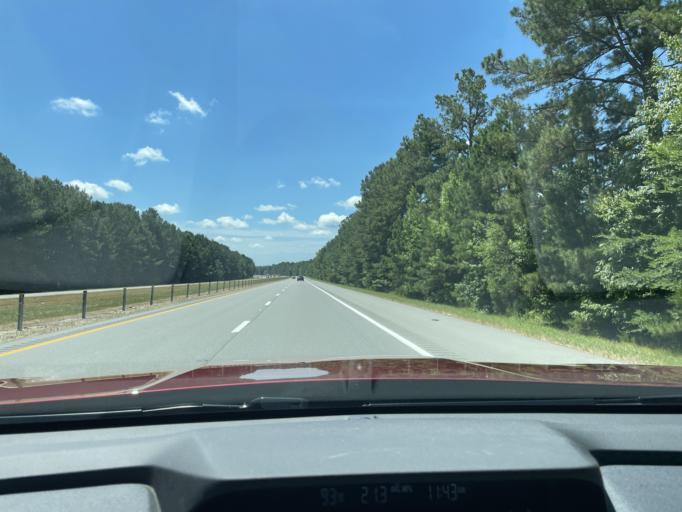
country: US
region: Arkansas
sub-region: Jefferson County
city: White Hall
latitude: 34.3167
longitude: -92.1480
